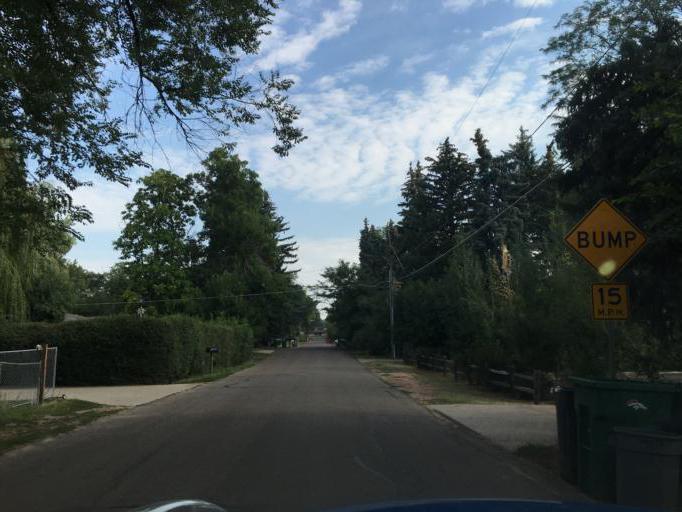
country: US
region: Colorado
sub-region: Jefferson County
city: Wheat Ridge
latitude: 39.7443
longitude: -105.1037
